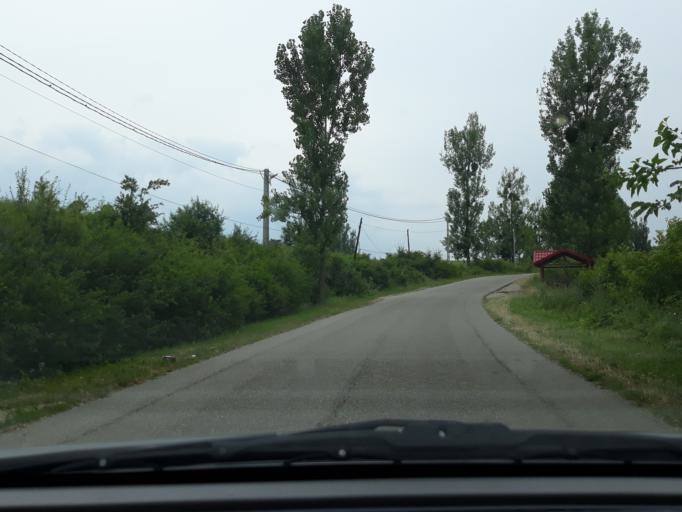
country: RO
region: Salaj
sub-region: Comuna Criseni
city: Criseni
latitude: 47.2469
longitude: 23.0701
